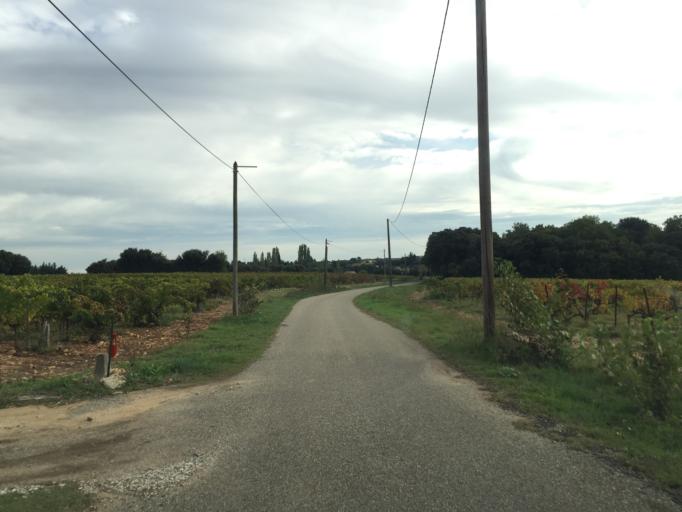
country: FR
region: Provence-Alpes-Cote d'Azur
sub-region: Departement du Vaucluse
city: Orange
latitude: 44.1122
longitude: 4.8139
